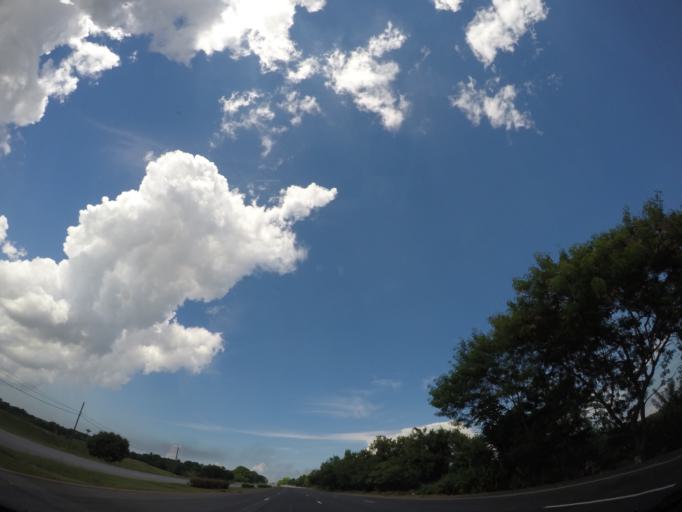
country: CU
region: La Habana
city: Havana
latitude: 23.1259
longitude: -82.3982
